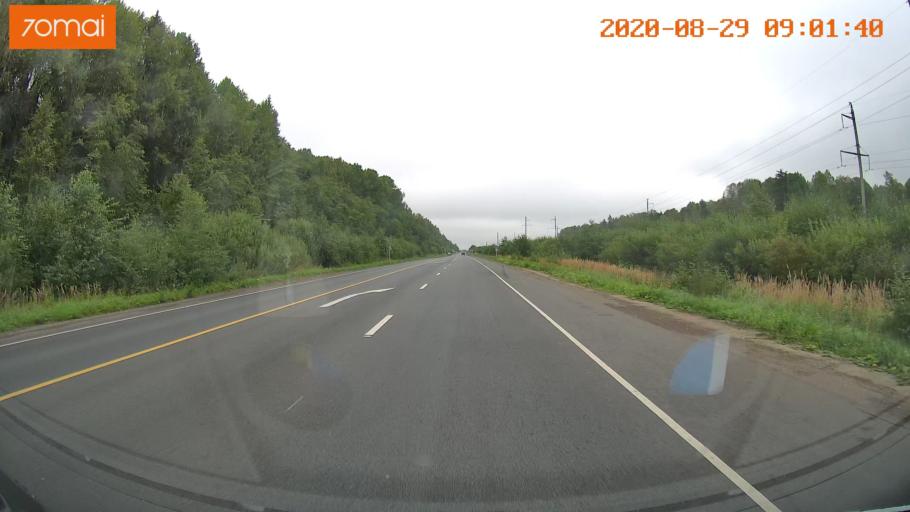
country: RU
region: Ivanovo
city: Staraya Vichuga
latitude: 57.3182
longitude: 41.9363
